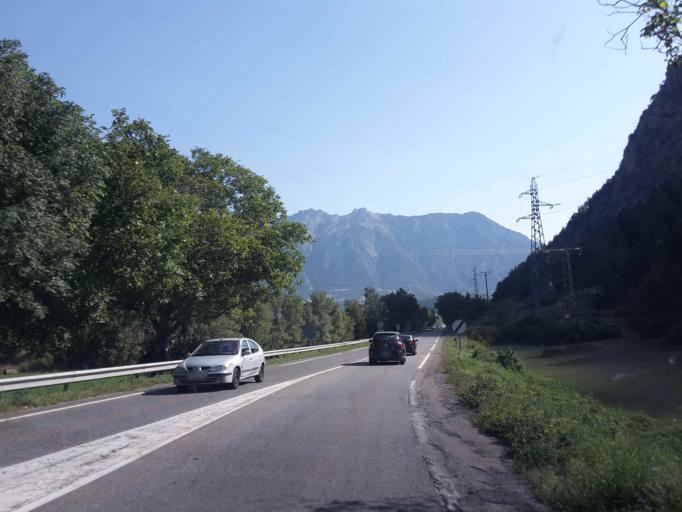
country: FR
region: Provence-Alpes-Cote d'Azur
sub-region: Departement des Hautes-Alpes
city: Guillestre
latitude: 44.6512
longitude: 6.5864
